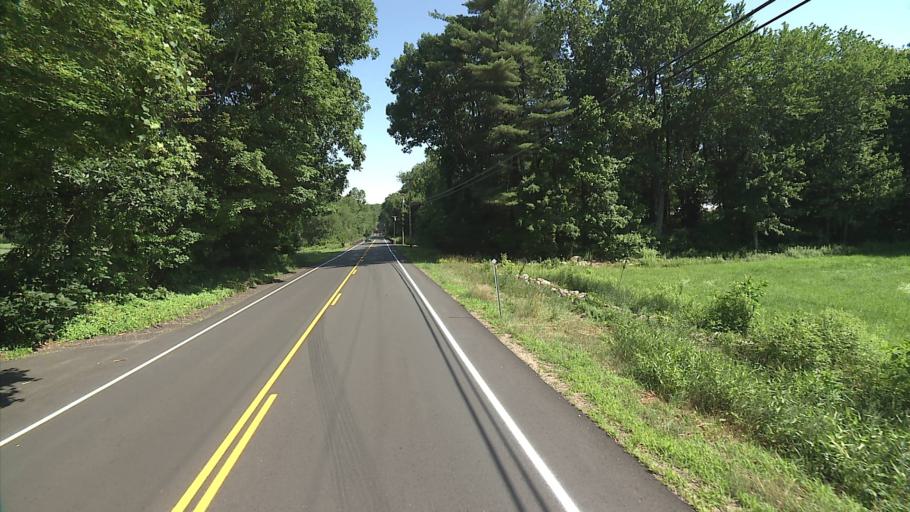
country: US
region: Connecticut
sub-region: Litchfield County
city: Northwest Harwinton
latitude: 41.7607
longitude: -73.0250
